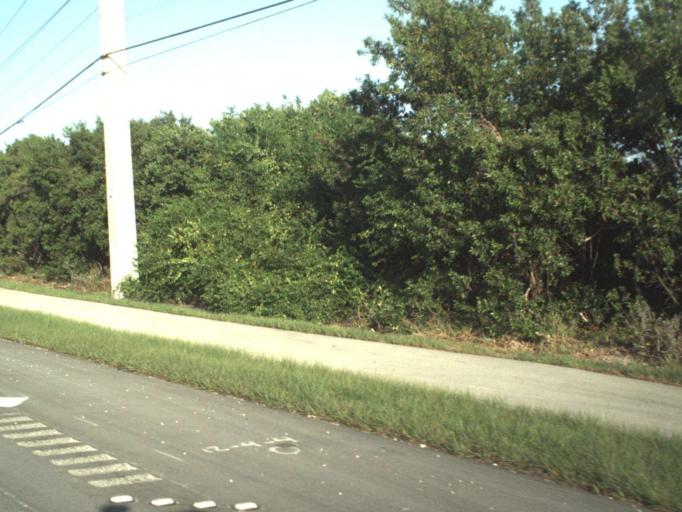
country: US
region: Florida
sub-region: Monroe County
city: Islamorada
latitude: 24.8408
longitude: -80.7891
